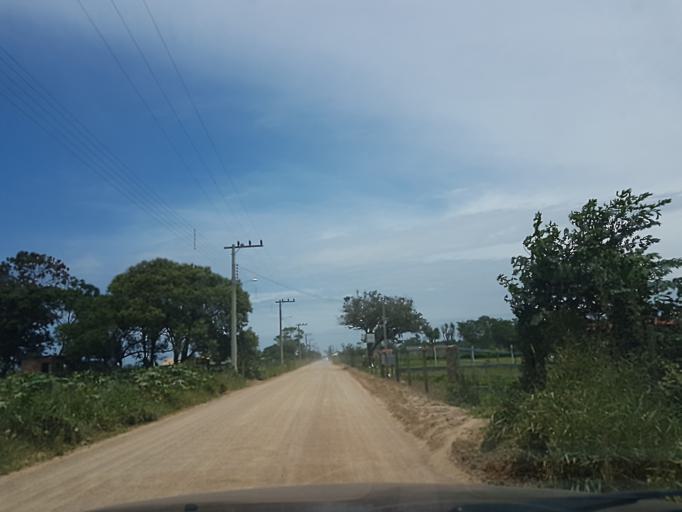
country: BR
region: Santa Catarina
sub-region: Jaguaruna
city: Jaguaruna
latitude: -28.6328
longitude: -48.9551
